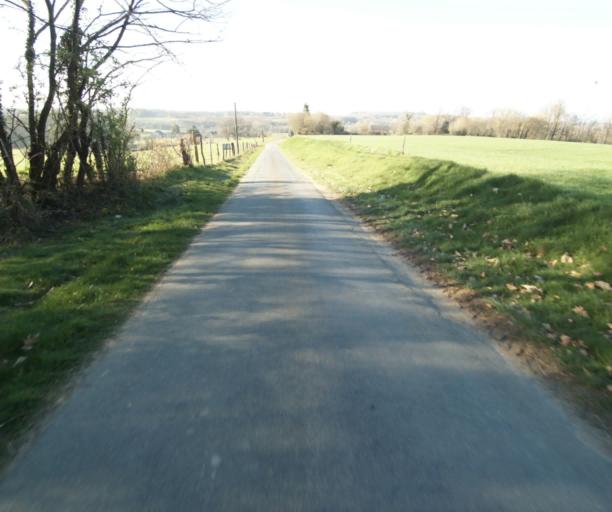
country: FR
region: Limousin
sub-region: Departement de la Correze
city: Uzerche
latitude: 45.3862
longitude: 1.5881
